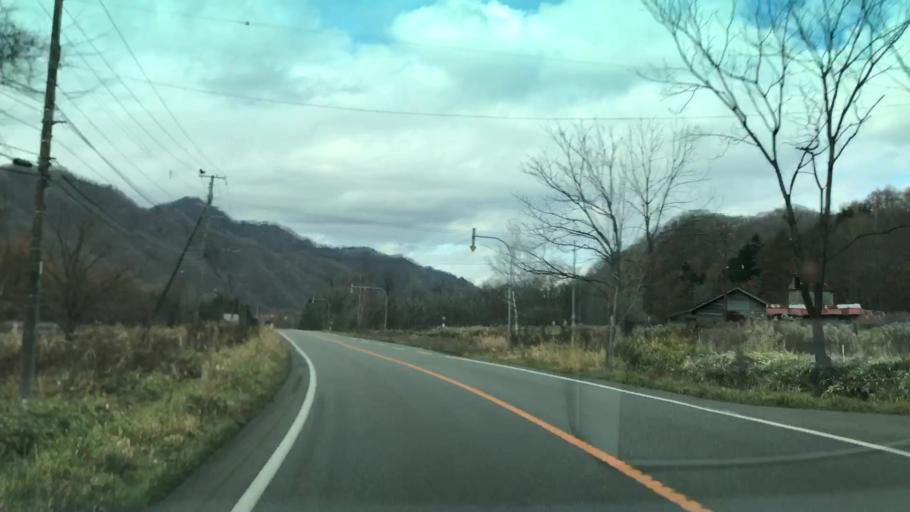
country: JP
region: Hokkaido
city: Shizunai-furukawacho
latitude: 42.8168
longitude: 142.4215
